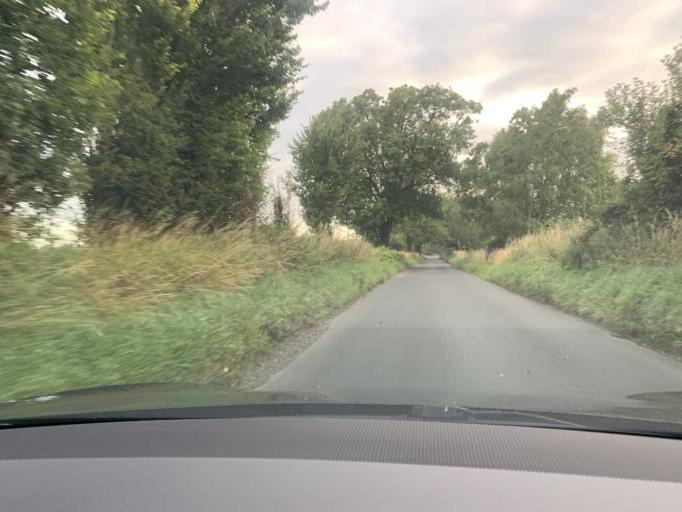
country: GB
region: England
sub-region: Wiltshire
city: Great Bedwyn
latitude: 51.3357
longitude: -1.6093
